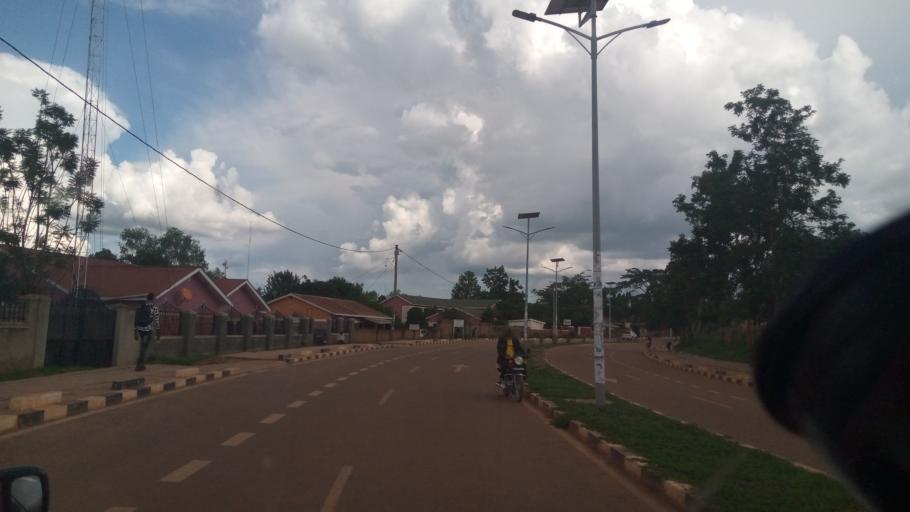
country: UG
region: Northern Region
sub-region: Lira District
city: Lira
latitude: 2.2409
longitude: 32.8996
